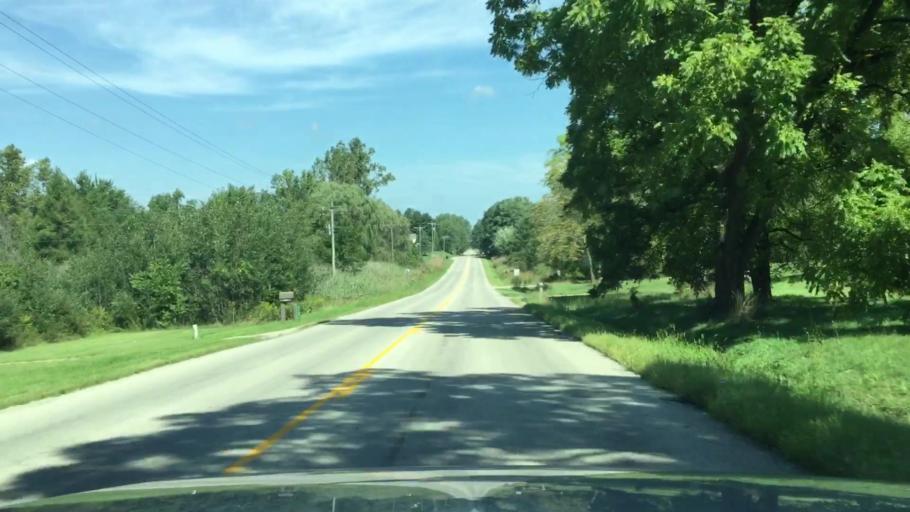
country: US
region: Michigan
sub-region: Lenawee County
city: Manitou Beach-Devils Lake
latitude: 42.0186
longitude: -84.2762
